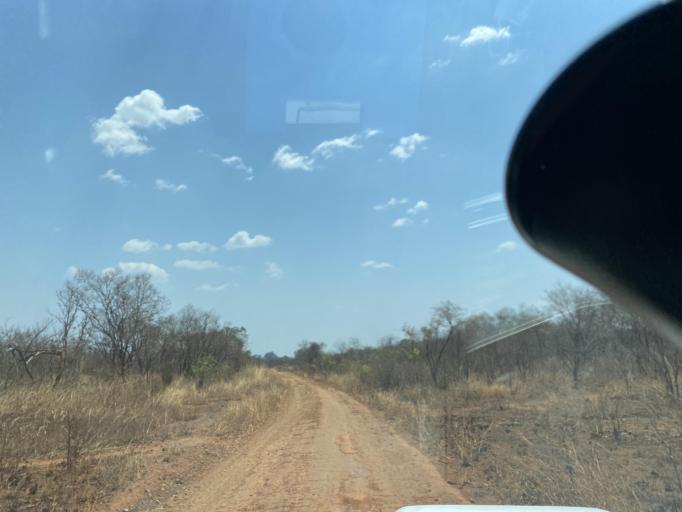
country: ZM
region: Lusaka
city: Lusaka
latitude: -15.5090
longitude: 27.9955
